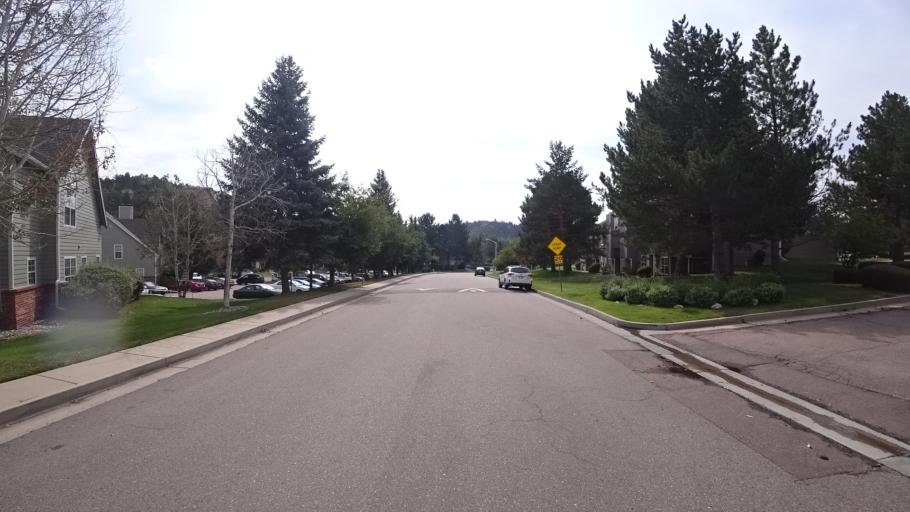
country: US
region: Colorado
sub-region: El Paso County
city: Colorado Springs
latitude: 38.8930
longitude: -104.7874
